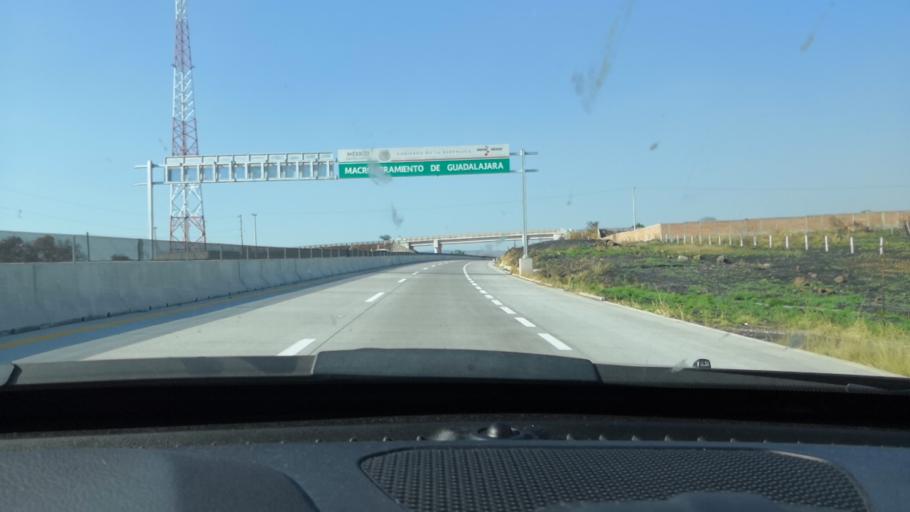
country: MX
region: Jalisco
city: Zapotlanejo
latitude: 20.6054
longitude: -103.1025
